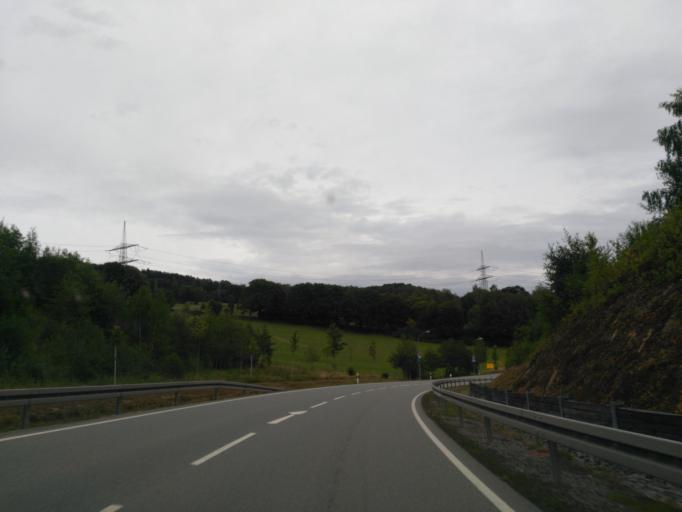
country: DE
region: Saxony
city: Markersbach
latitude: 50.5376
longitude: 12.8757
